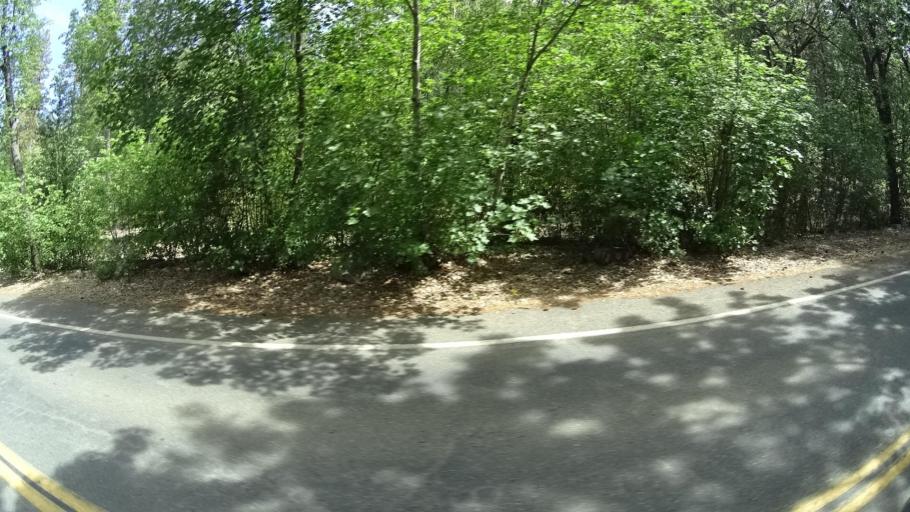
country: US
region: California
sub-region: Lake County
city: Cobb
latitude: 38.8628
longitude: -122.7165
